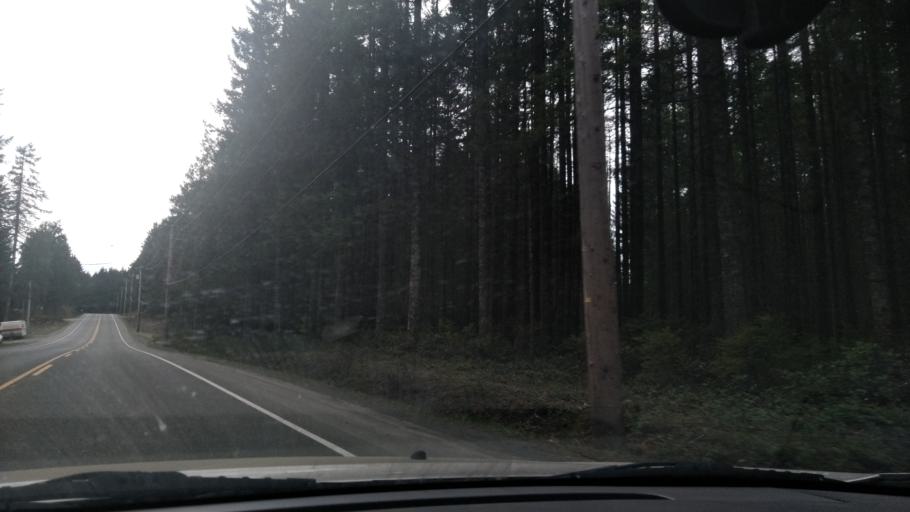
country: CA
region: British Columbia
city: Campbell River
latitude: 50.0140
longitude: -125.3554
